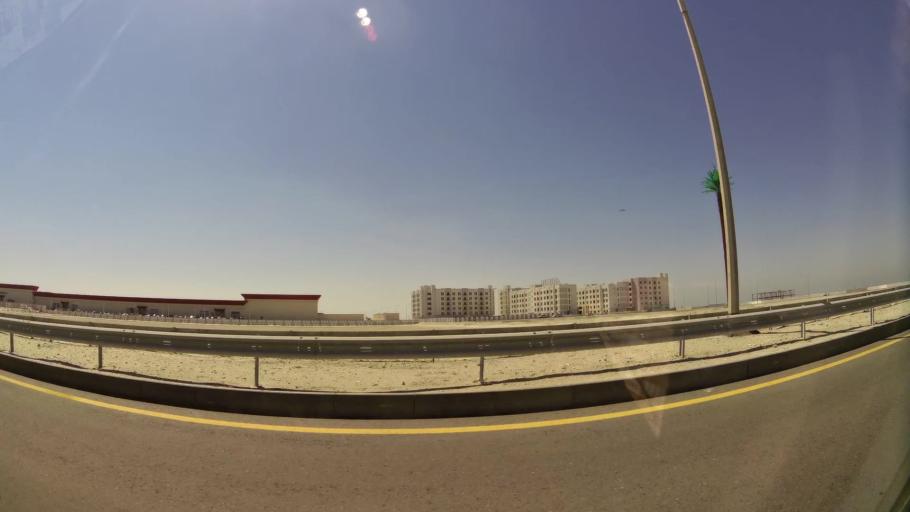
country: BH
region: Muharraq
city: Al Muharraq
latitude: 26.3093
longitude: 50.6246
